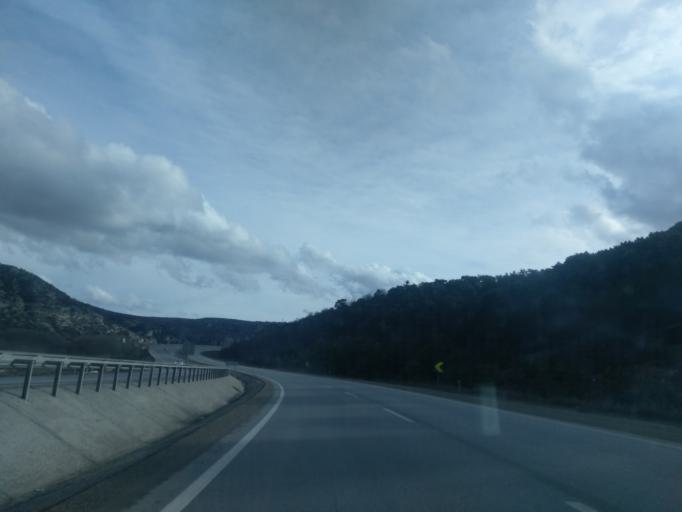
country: TR
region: Kuetahya
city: Sabuncu
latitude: 39.5647
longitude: 30.0724
